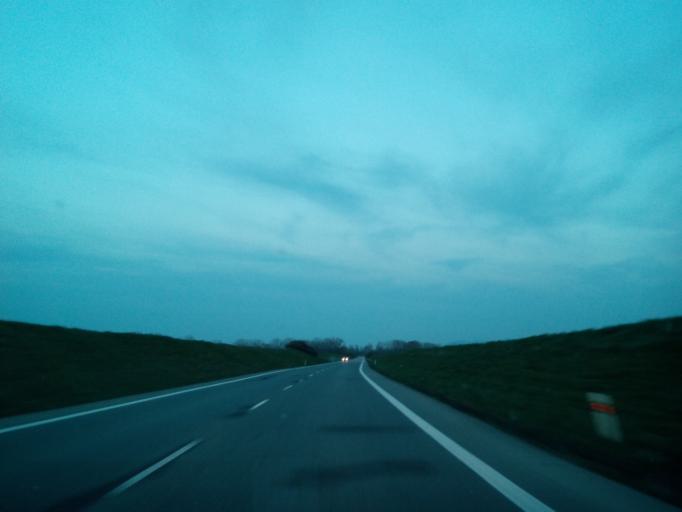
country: SK
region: Kosicky
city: Moldava nad Bodvou
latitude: 48.6031
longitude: 21.0221
